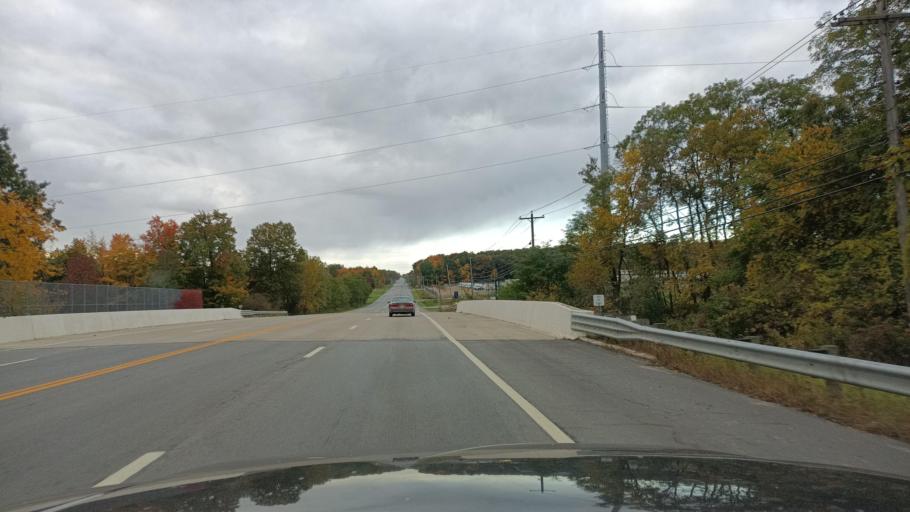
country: US
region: Ohio
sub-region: Trumbull County
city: Lordstown
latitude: 41.1540
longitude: -80.8571
